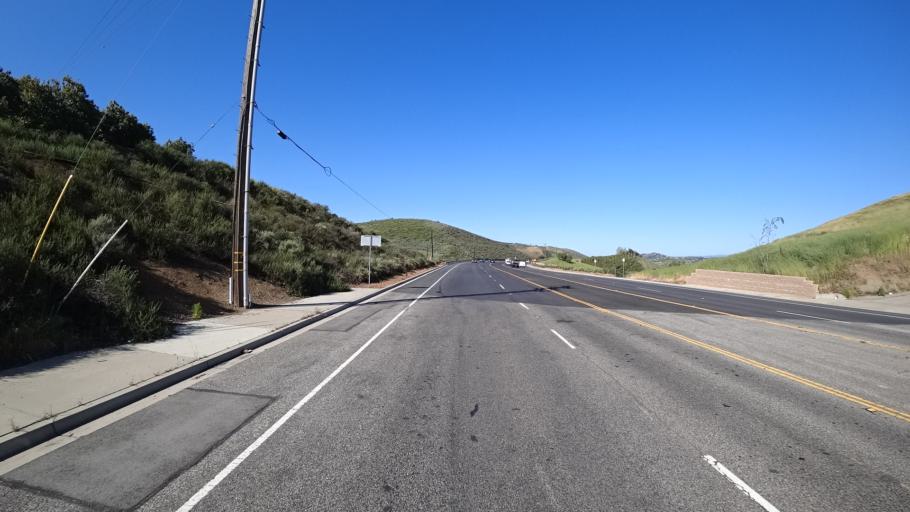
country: US
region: California
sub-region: Ventura County
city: Simi Valley
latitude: 34.2506
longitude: -118.8246
